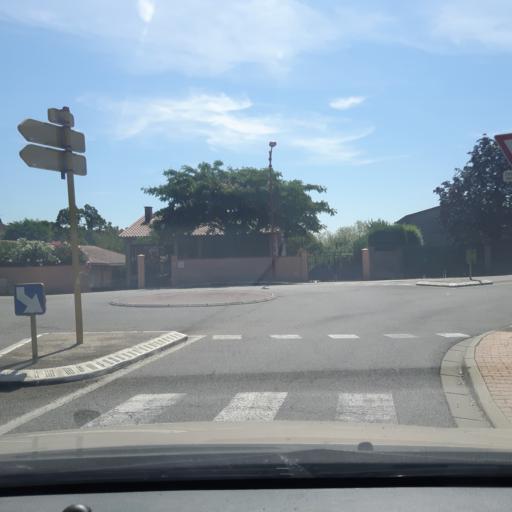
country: FR
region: Midi-Pyrenees
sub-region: Departement de la Haute-Garonne
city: Bouloc
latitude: 43.7810
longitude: 1.4031
